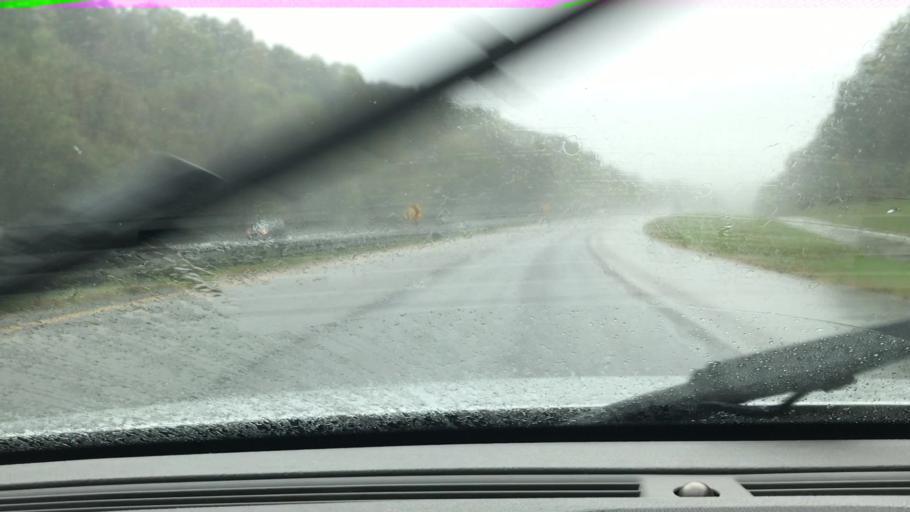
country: US
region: Alabama
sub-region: Limestone County
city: Ardmore
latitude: 34.9856
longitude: -86.8805
